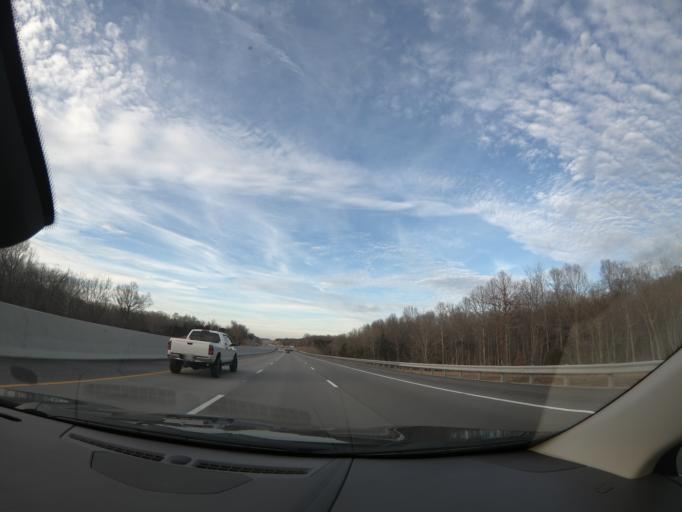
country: US
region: Kentucky
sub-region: Hart County
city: Munfordville
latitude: 37.4071
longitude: -85.8813
